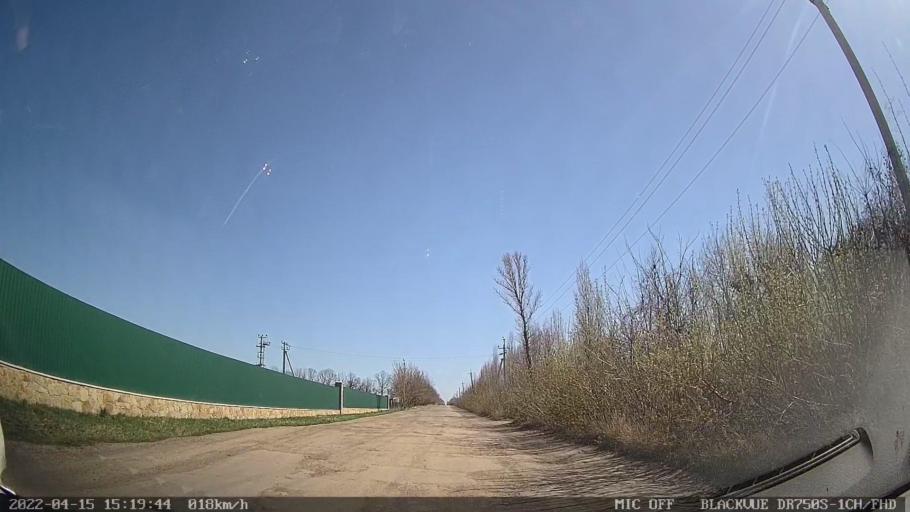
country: MD
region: Raionul Ocnita
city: Otaci
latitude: 48.3875
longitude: 27.9060
